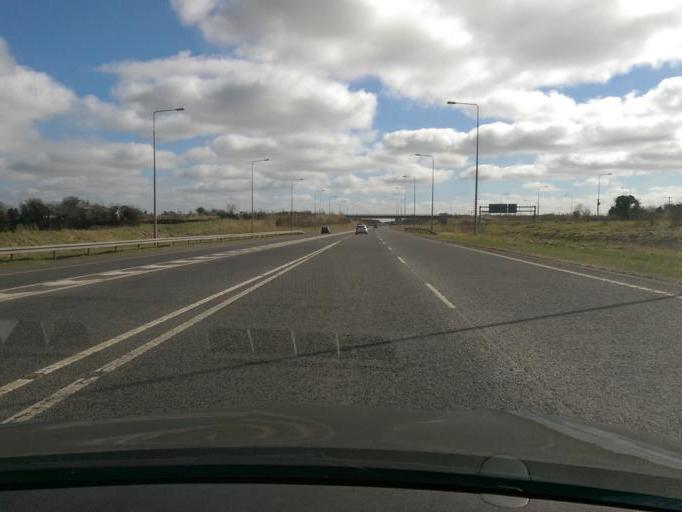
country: IE
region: Leinster
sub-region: An Iarmhi
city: Kinnegad
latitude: 53.4503
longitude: -7.1008
